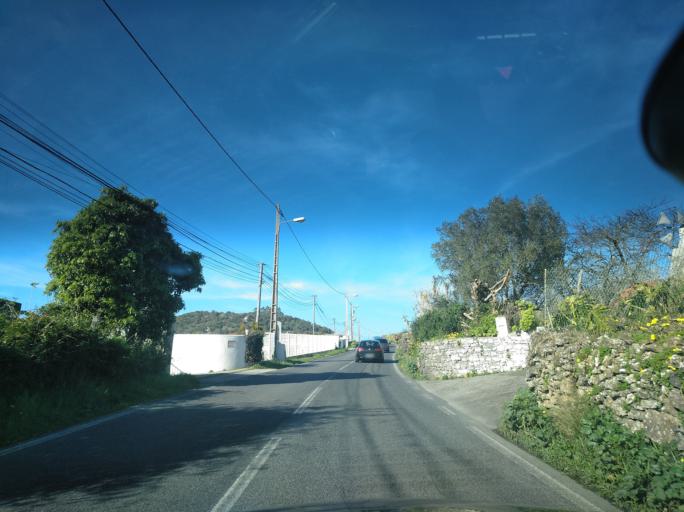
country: PT
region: Lisbon
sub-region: Sintra
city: Pero Pinheiro
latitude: 38.8936
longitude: -9.3268
